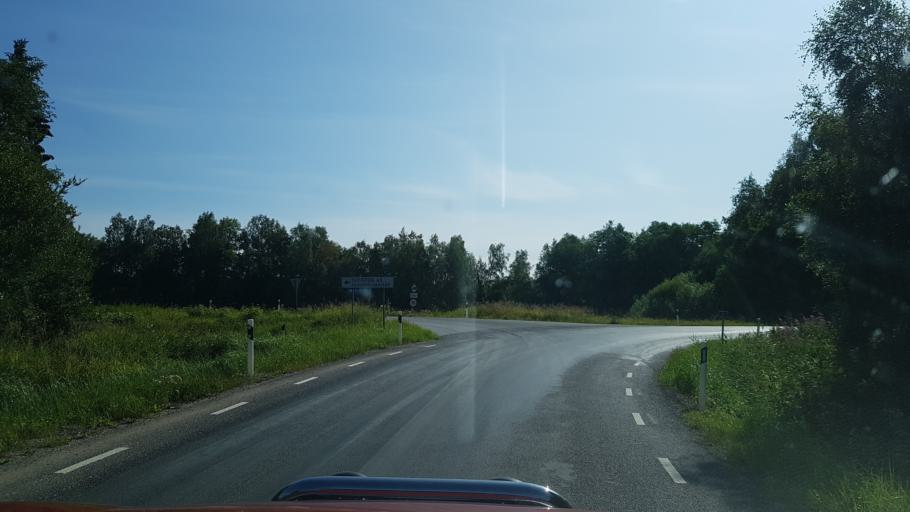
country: EE
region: Harju
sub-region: Rae vald
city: Vaida
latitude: 59.2623
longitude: 25.0488
